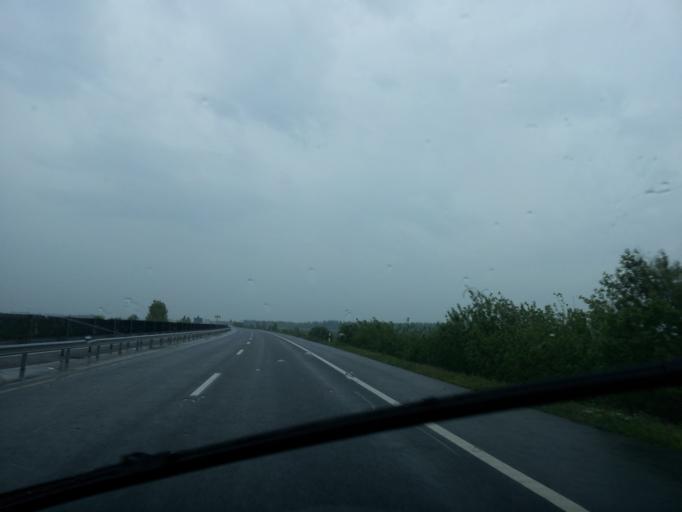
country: HU
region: Tolna
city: Ocseny
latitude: 46.3512
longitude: 18.7575
